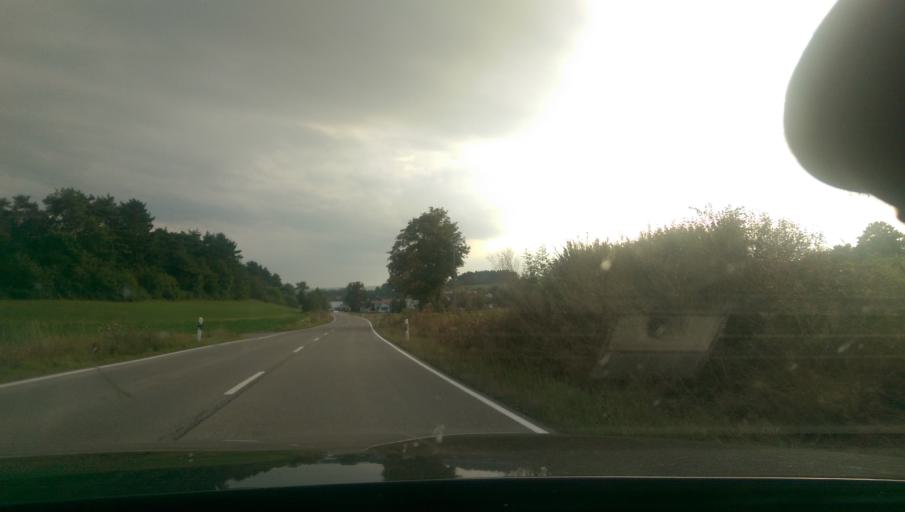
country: DE
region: Baden-Wuerttemberg
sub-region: Karlsruhe Region
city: Heimsheim
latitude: 48.8208
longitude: 8.8665
